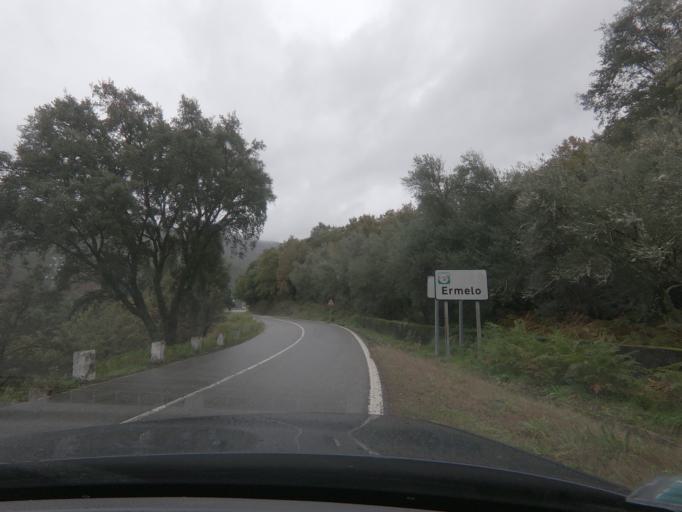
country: PT
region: Vila Real
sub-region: Mondim de Basto
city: Mondim de Basto
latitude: 41.3508
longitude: -7.8894
